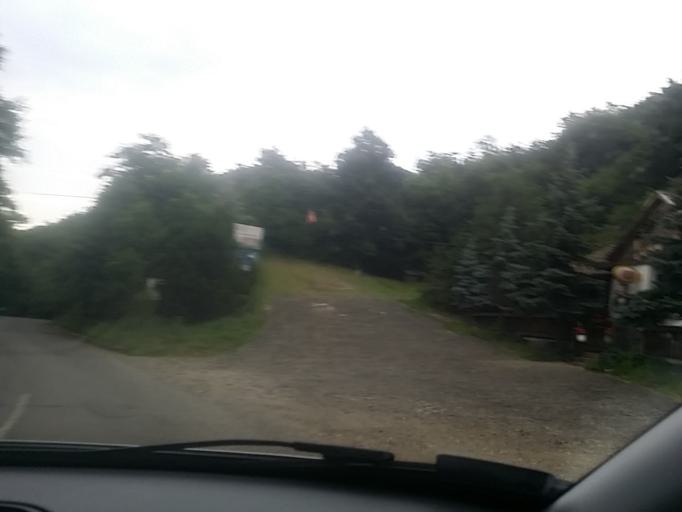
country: HU
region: Nograd
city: Bujak
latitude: 47.9382
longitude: 19.6080
